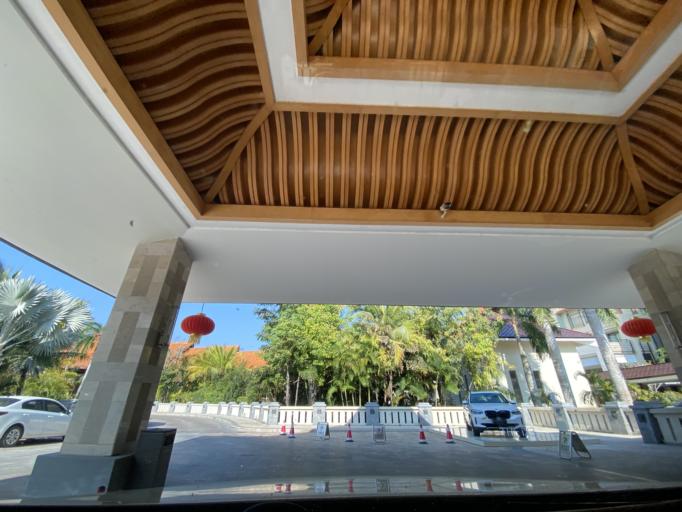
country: CN
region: Hainan
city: Haitangwan
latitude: 18.4023
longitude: 109.7803
